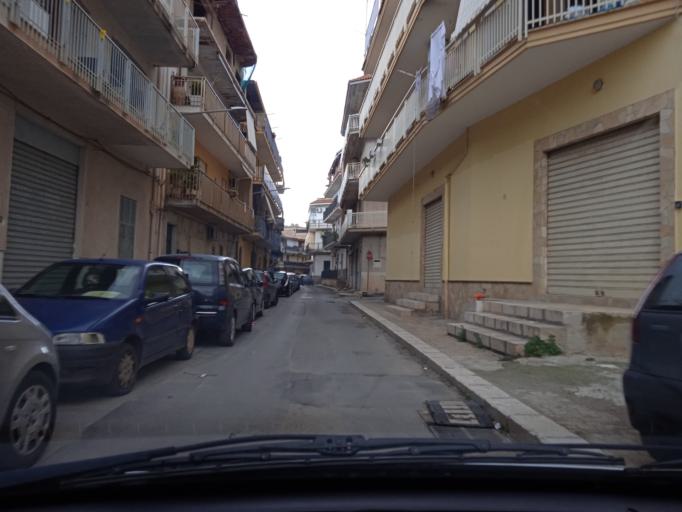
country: IT
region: Sicily
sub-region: Palermo
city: Villabate
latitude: 38.0741
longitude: 13.4487
